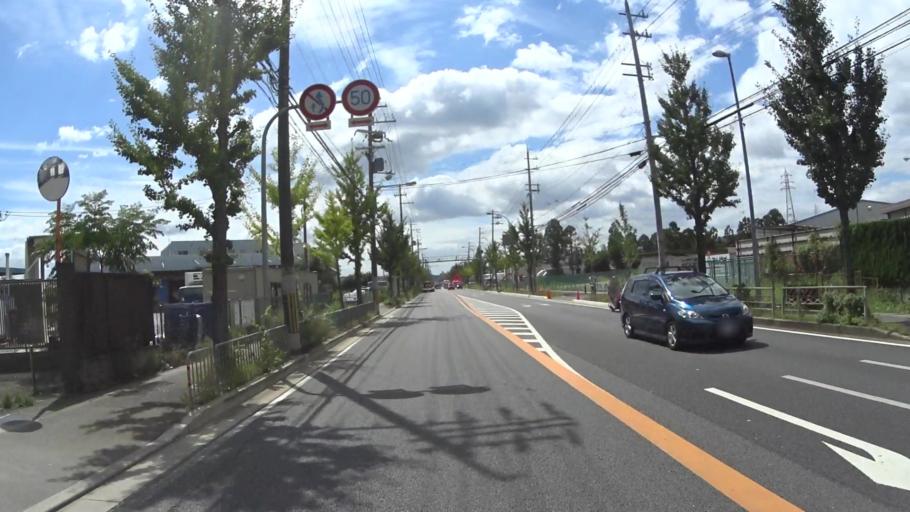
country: JP
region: Kyoto
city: Muko
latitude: 34.9202
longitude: 135.7318
